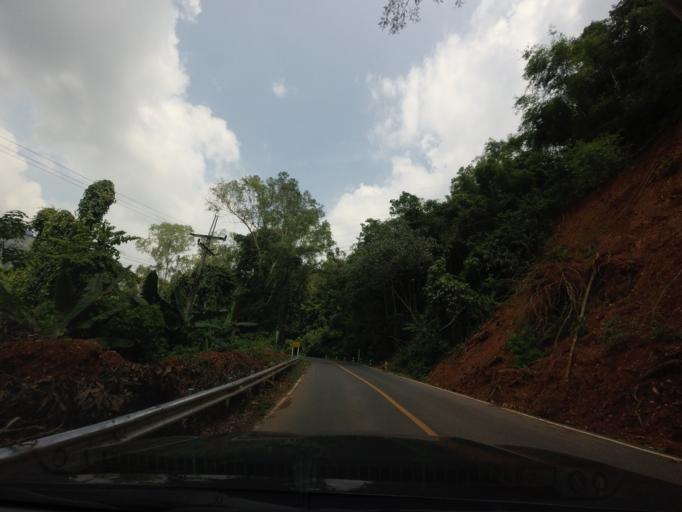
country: TH
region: Nan
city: Pua
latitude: 19.1834
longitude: 100.9913
